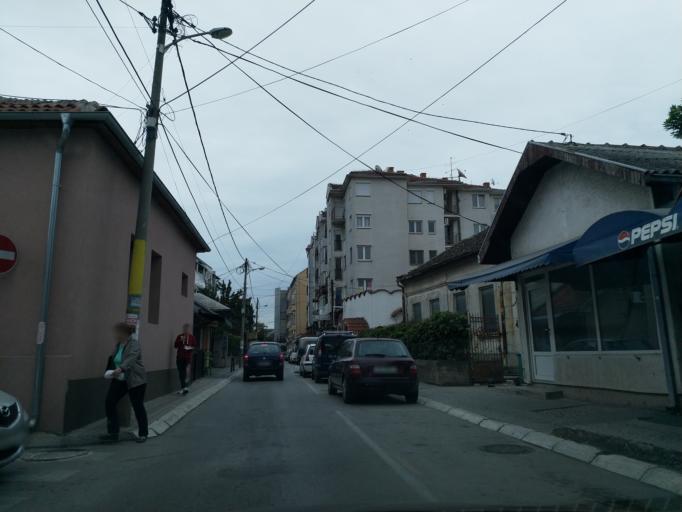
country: RS
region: Central Serbia
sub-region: Pomoravski Okrug
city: Paracin
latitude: 43.8588
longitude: 21.4092
